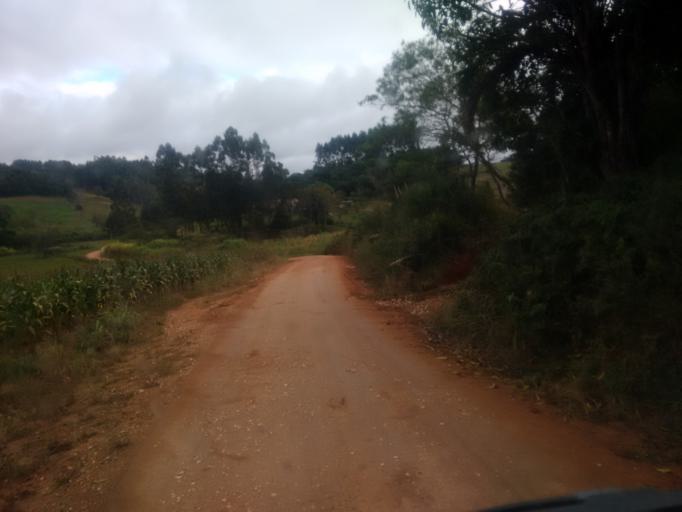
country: BR
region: Rio Grande do Sul
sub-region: Camaqua
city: Camaqua
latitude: -30.7220
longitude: -51.8678
